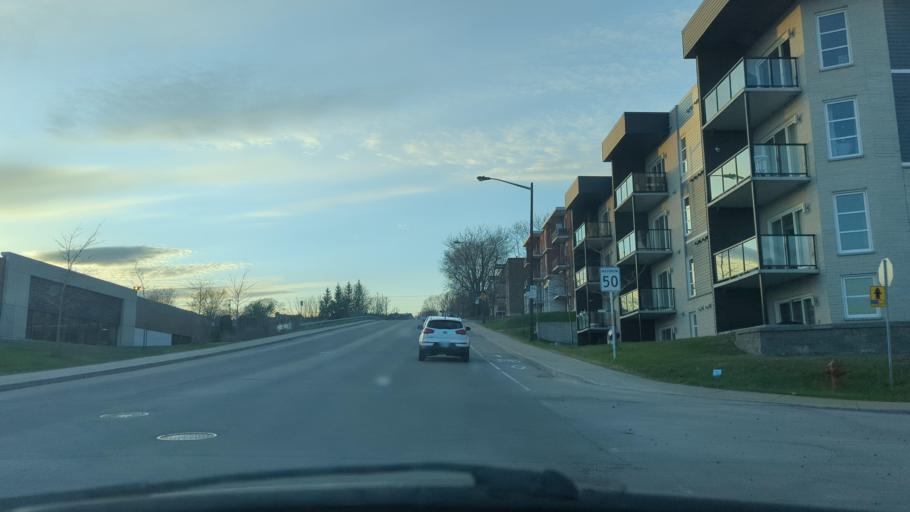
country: CA
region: Quebec
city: Quebec
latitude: 46.8480
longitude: -71.2599
